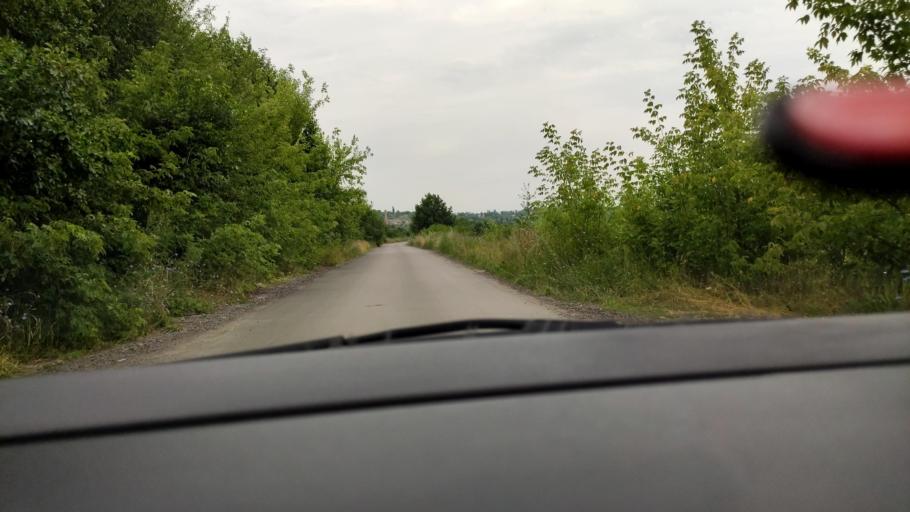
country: RU
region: Voronezj
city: Ramon'
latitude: 51.8963
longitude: 39.3513
